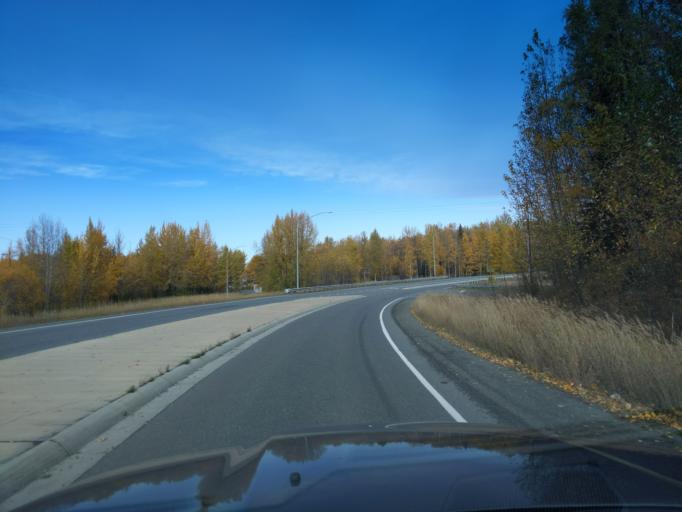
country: US
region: Alaska
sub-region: Anchorage Municipality
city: Anchorage
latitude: 61.1650
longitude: -149.9521
